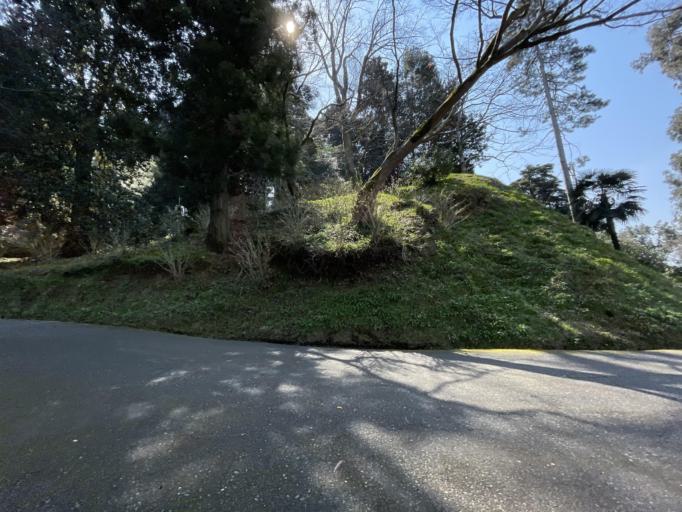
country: GE
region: Ajaria
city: Makhinjauri
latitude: 41.6978
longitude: 41.7143
